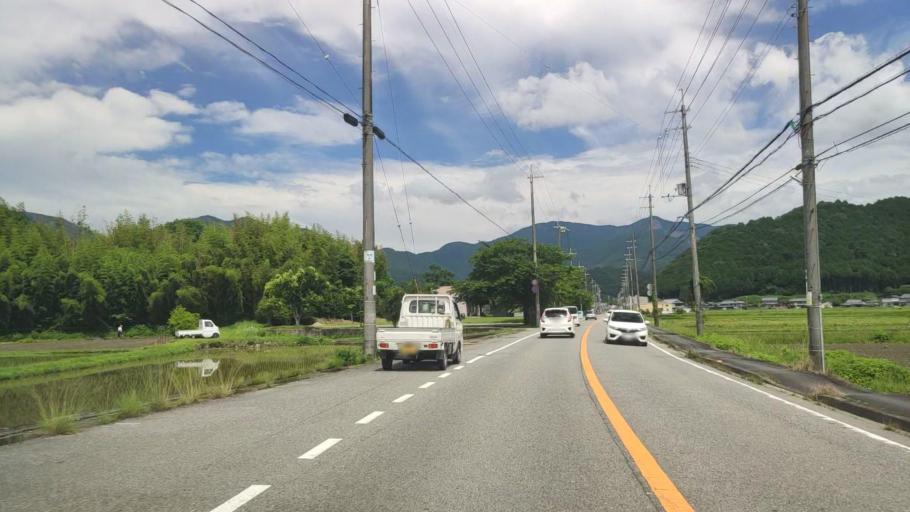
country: JP
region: Hyogo
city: Nishiwaki
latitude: 35.0740
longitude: 134.8993
